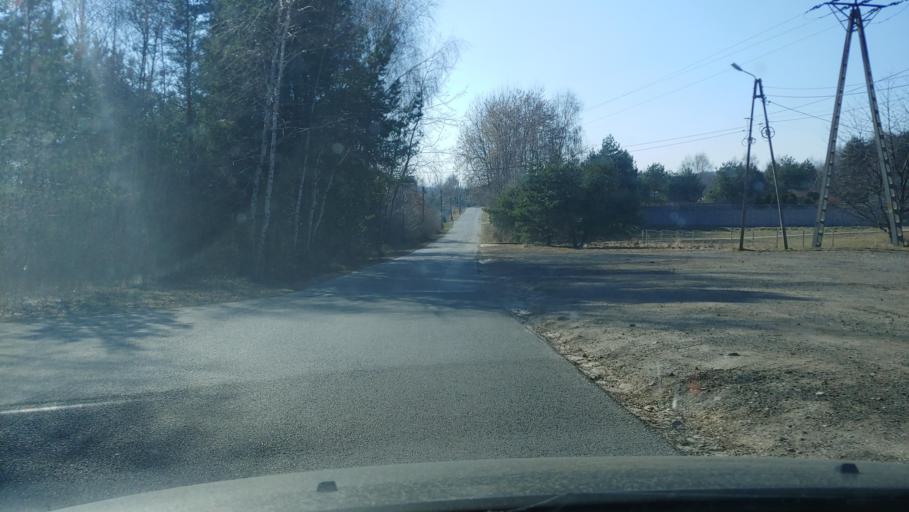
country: PL
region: Lesser Poland Voivodeship
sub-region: Powiat chrzanowski
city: Myslachowice
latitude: 50.1811
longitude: 19.4704
